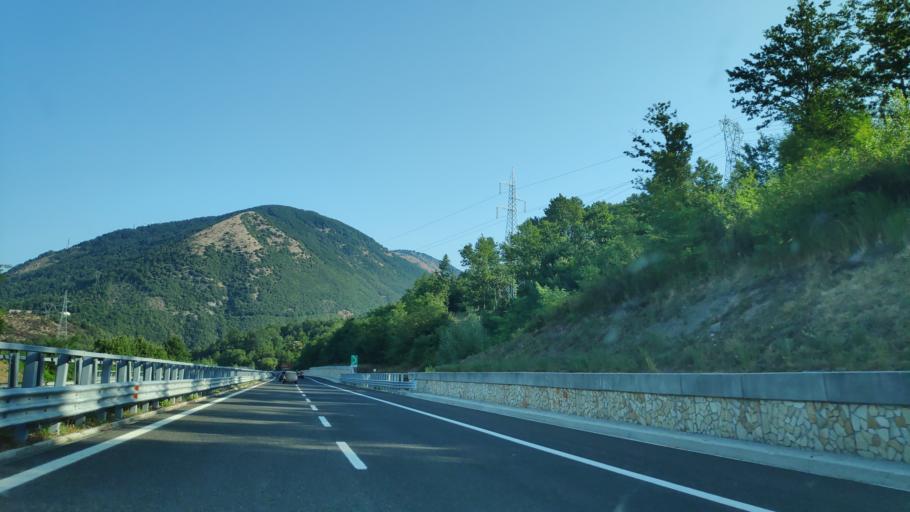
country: IT
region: Basilicate
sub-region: Provincia di Potenza
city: Lagonegro
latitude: 40.1182
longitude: 15.7846
